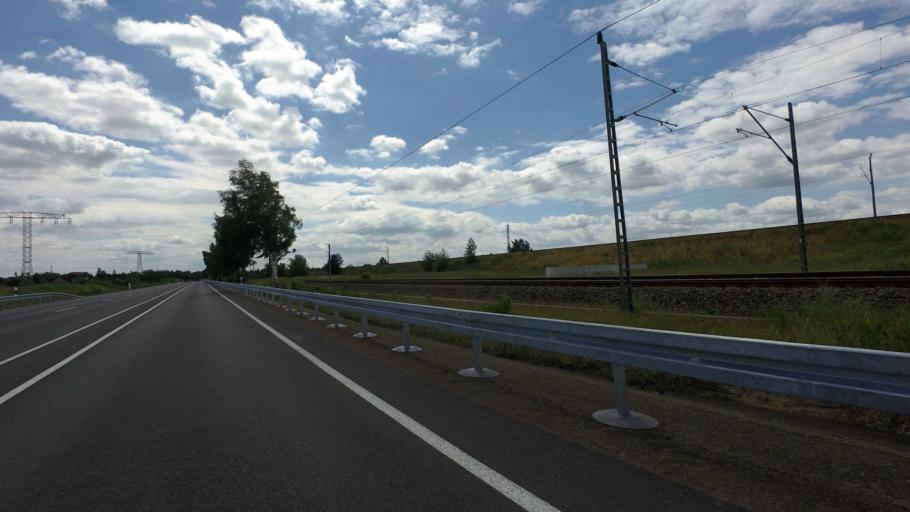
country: DE
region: Brandenburg
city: Grossraschen
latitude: 51.5610
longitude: 14.0622
